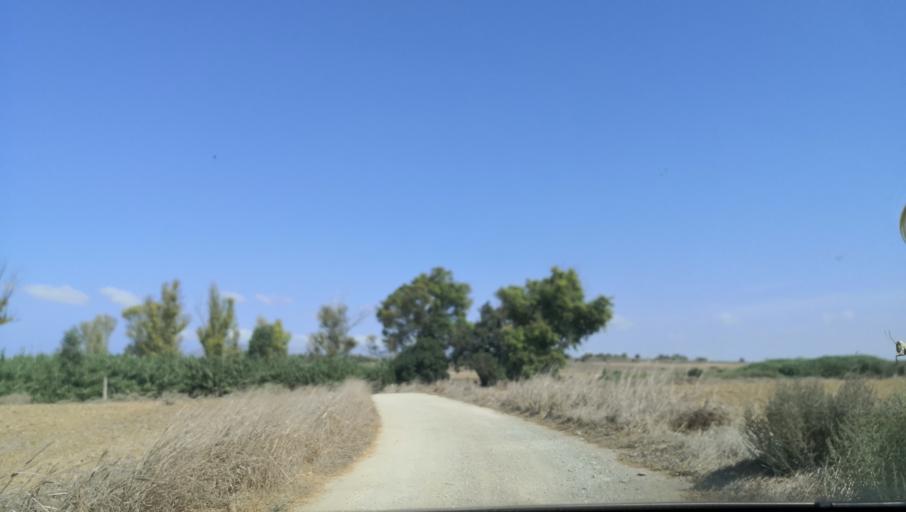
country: CY
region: Lefkosia
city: Mammari
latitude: 35.1788
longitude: 33.2271
